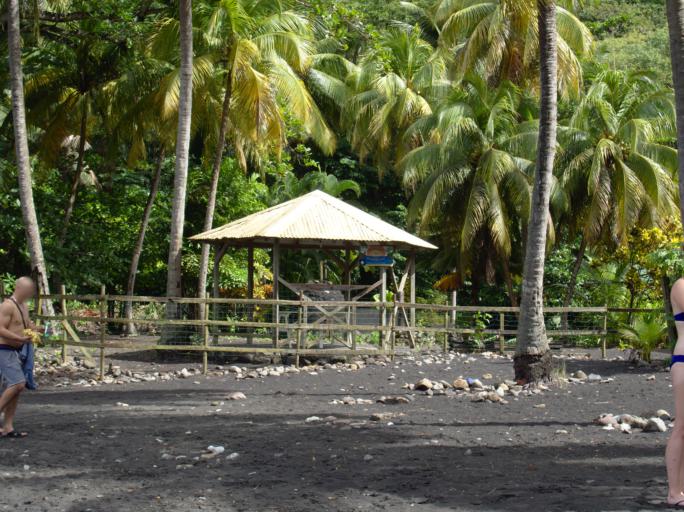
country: MQ
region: Martinique
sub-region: Martinique
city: Les Trois-Ilets
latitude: 14.5278
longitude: -61.0872
